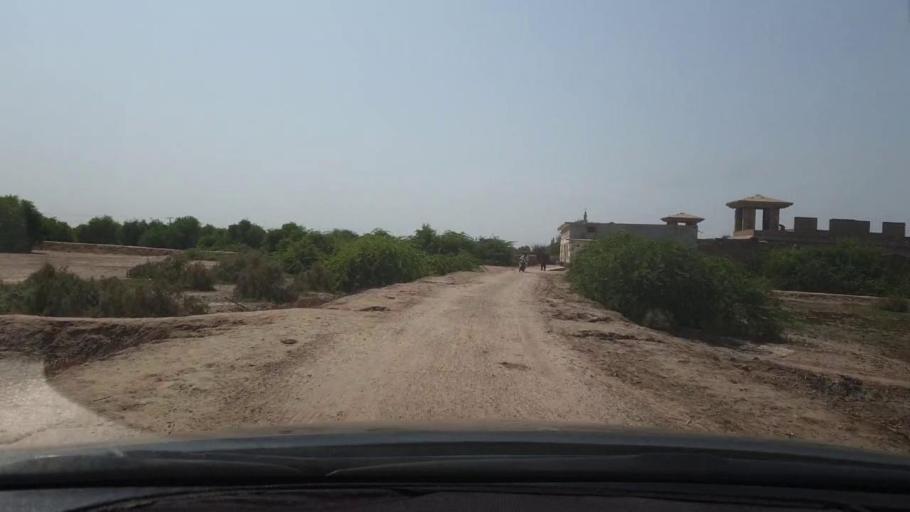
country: PK
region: Sindh
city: Naukot
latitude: 24.8060
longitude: 69.2439
